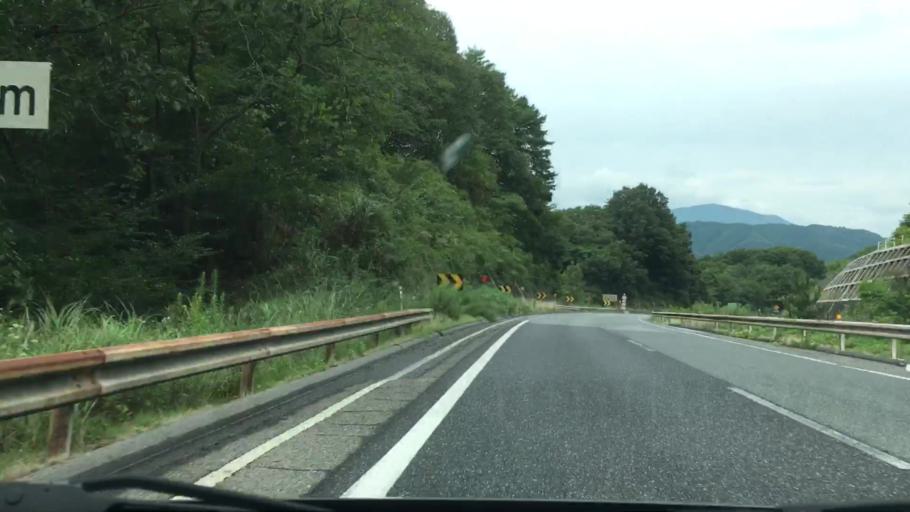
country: JP
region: Okayama
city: Niimi
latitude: 35.0142
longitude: 133.5853
